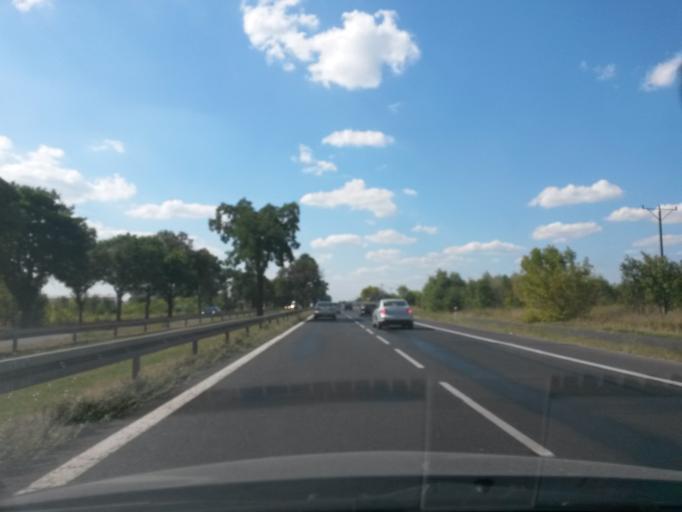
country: PL
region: Masovian Voivodeship
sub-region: Powiat nowodworski
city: Nowy Dwor Mazowiecki
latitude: 52.3788
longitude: 20.7694
